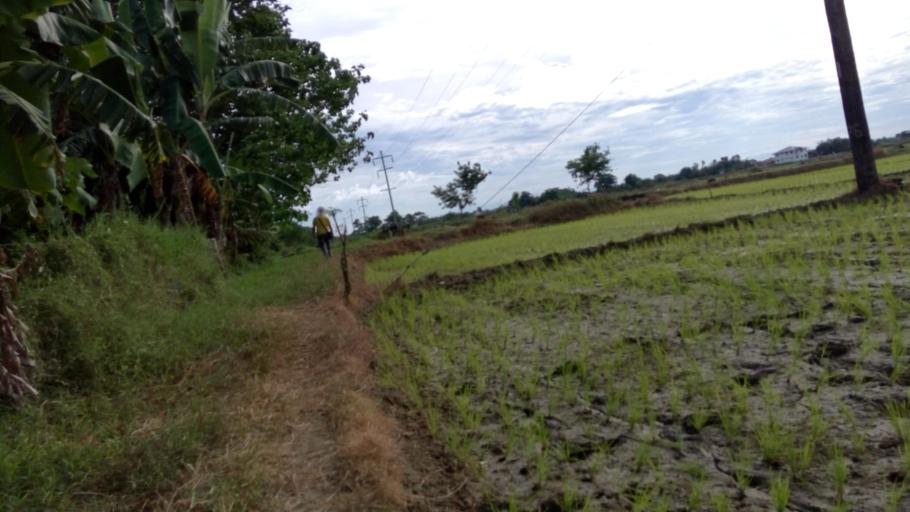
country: PH
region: Ilocos
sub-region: Province of La Union
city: San Eugenio
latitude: 16.3454
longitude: 120.3528
